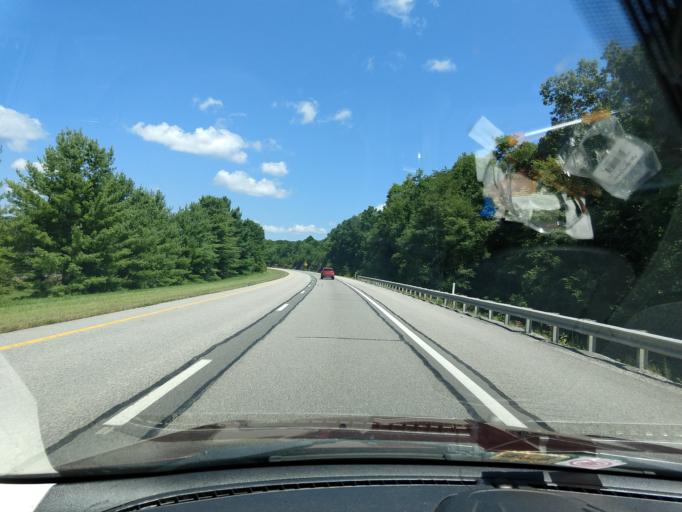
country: US
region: West Virginia
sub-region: Fayette County
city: Ansted
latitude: 38.1007
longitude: -81.0238
